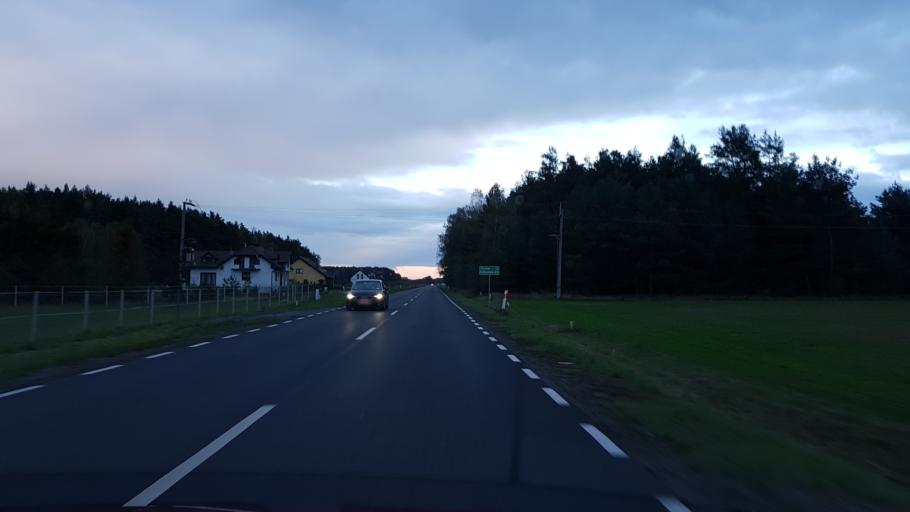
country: PL
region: Greater Poland Voivodeship
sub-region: Powiat zlotowski
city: Krajenka
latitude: 53.2665
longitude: 16.9275
